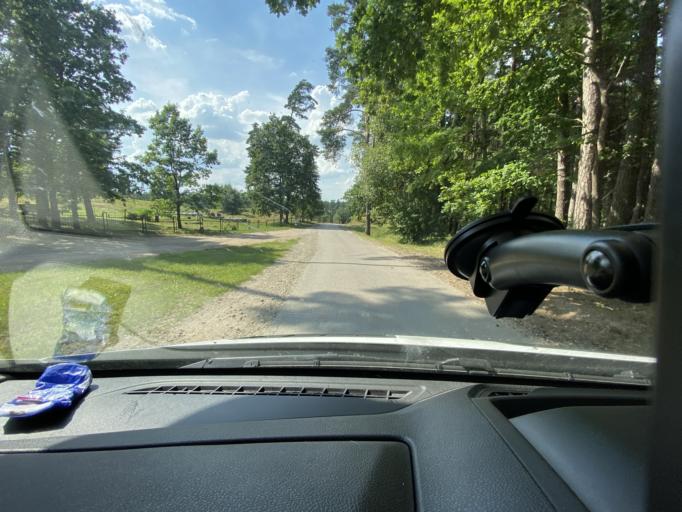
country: LT
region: Kauno apskritis
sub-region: Kauno rajonas
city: Karmelava
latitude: 54.9746
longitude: 24.0441
